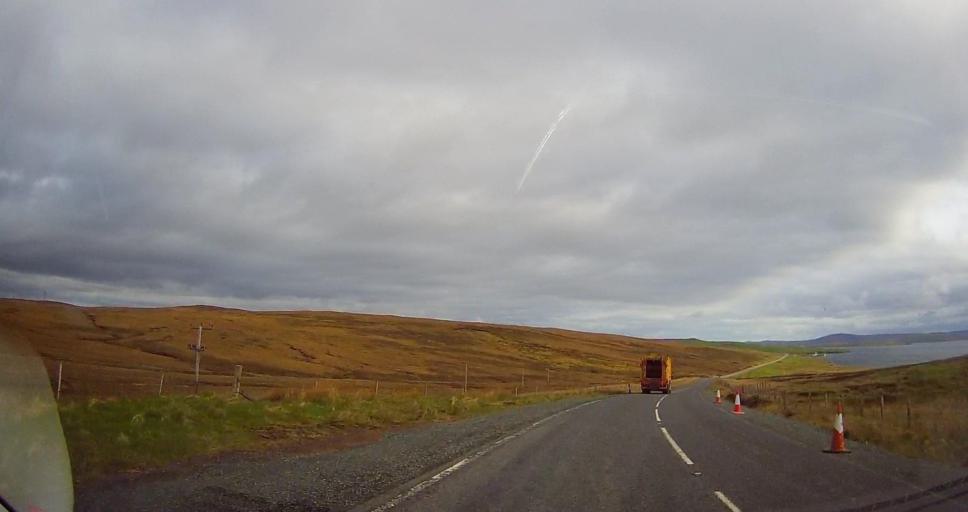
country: GB
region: Scotland
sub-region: Shetland Islands
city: Lerwick
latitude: 60.4497
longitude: -1.2130
